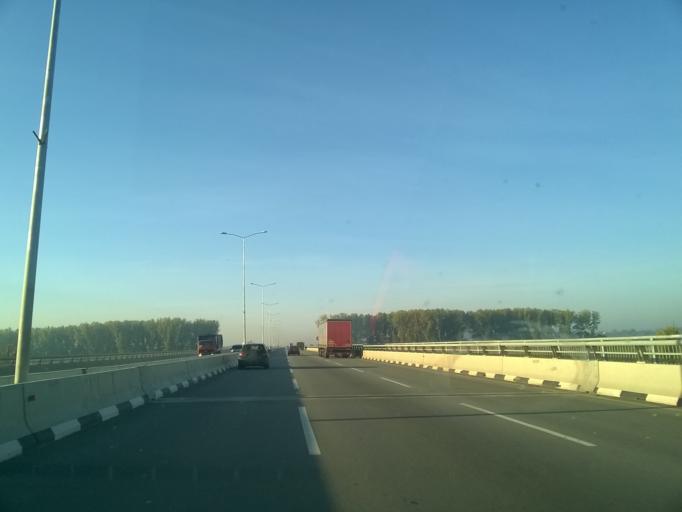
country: RS
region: Central Serbia
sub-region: Belgrade
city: Zemun
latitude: 44.8706
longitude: 20.3862
